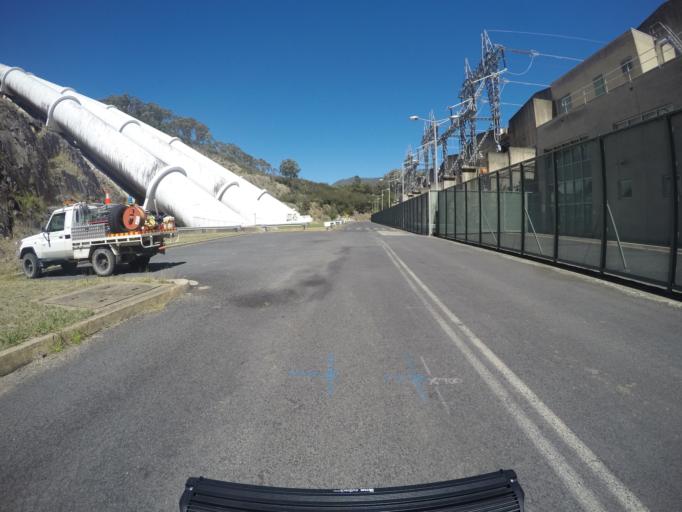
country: AU
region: New South Wales
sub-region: Tumut Shire
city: Tumut
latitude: -35.6110
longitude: 148.2923
